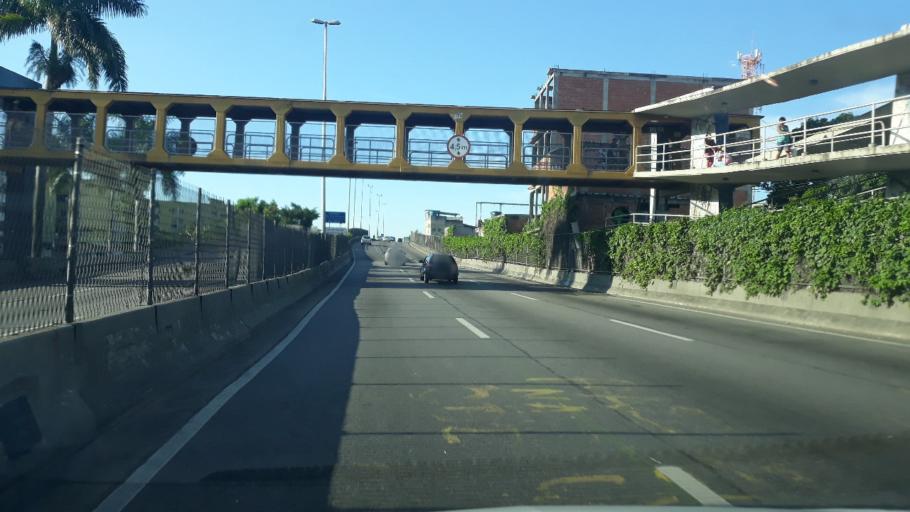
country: BR
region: Rio de Janeiro
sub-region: Sao Joao De Meriti
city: Sao Joao de Meriti
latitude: -22.9513
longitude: -43.3569
